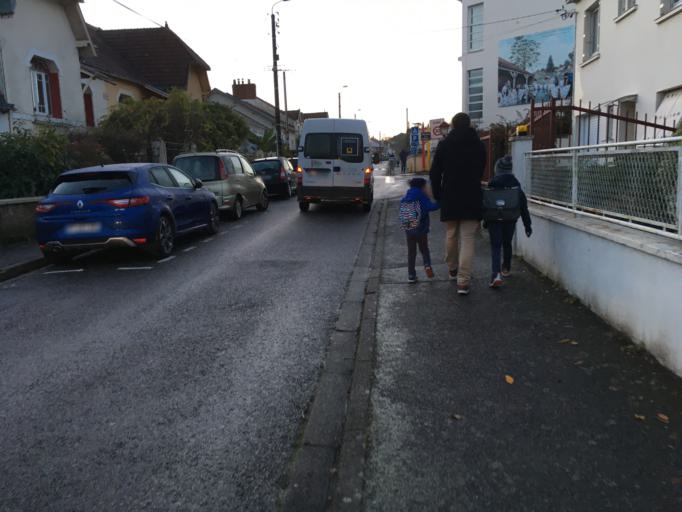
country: FR
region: Pays de la Loire
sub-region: Departement de la Loire-Atlantique
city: Saint-Sebastien-sur-Loire
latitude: 47.1923
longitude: -1.5194
